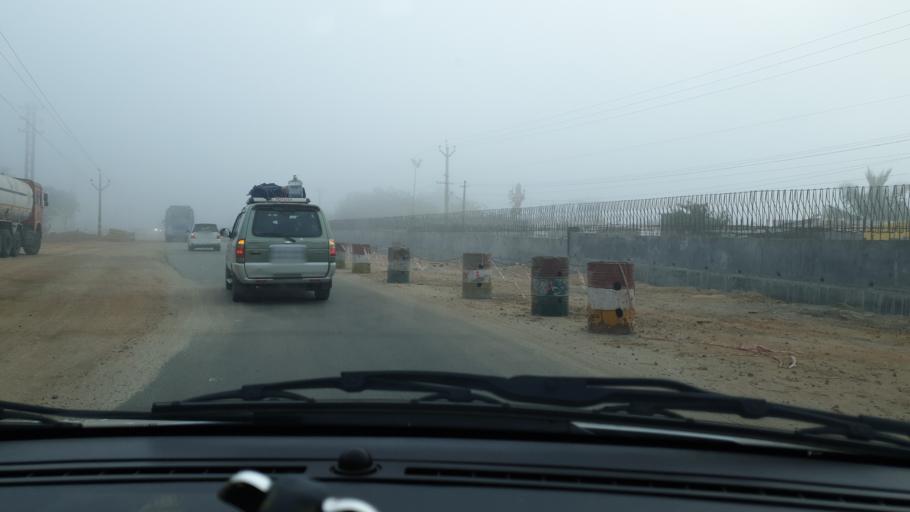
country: IN
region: Telangana
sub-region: Mahbubnagar
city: Nagar Karnul
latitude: 16.6615
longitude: 78.5314
